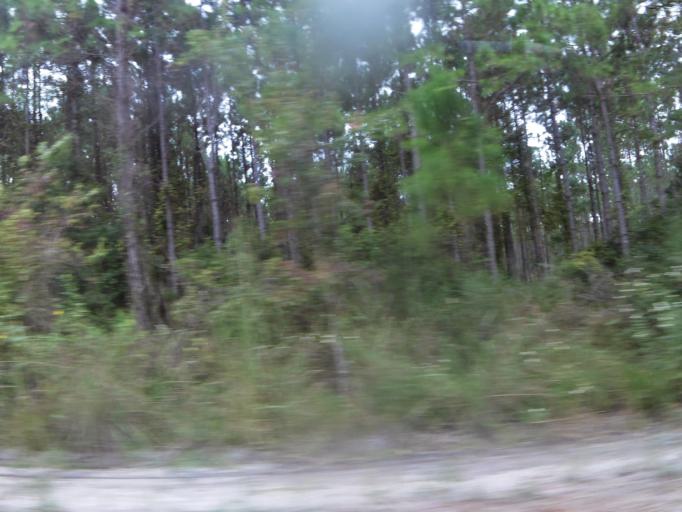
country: US
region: Florida
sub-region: Flagler County
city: Palm Coast
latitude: 29.5976
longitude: -81.3560
